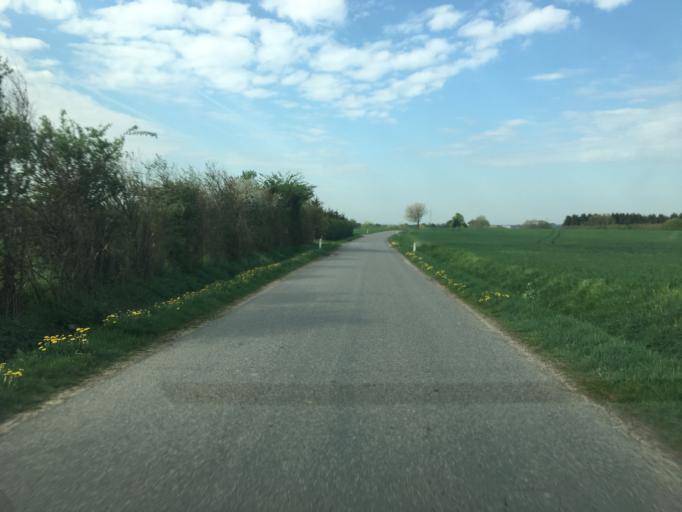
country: DK
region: South Denmark
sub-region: Haderslev Kommune
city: Haderslev
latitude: 55.2798
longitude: 9.4503
